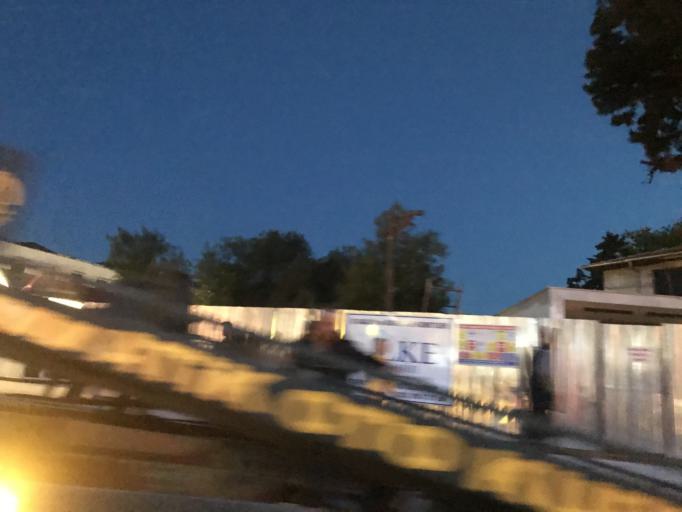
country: TR
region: Hatay
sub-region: Antakya Ilcesi
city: Antakya
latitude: 36.2024
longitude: 36.1604
